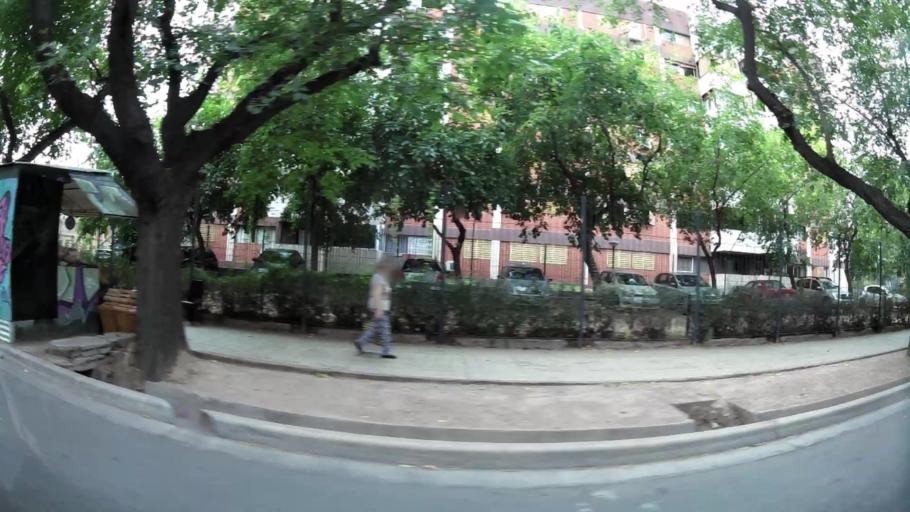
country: AR
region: Mendoza
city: Mendoza
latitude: -32.8765
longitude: -68.8450
